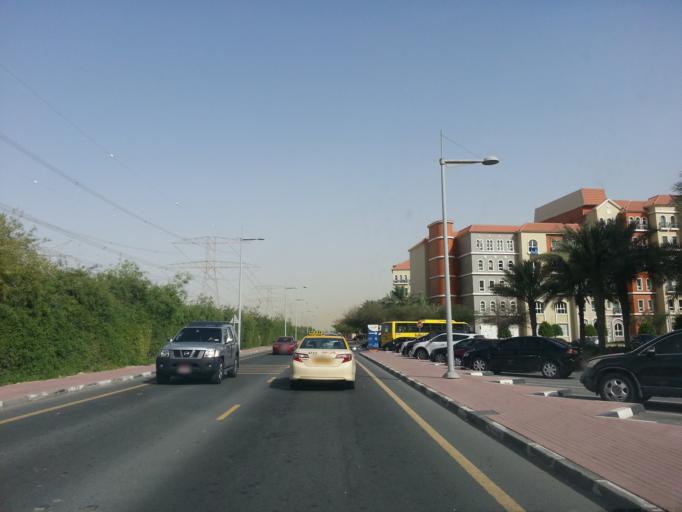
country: AE
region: Dubai
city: Dubai
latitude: 25.0424
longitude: 55.1447
